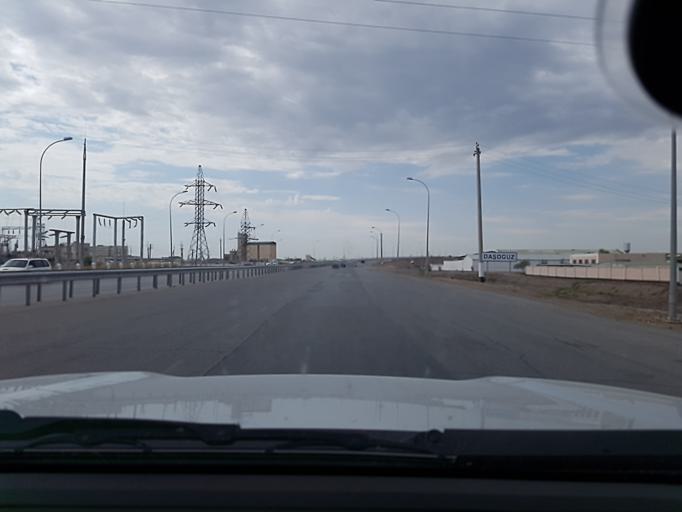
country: TM
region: Dasoguz
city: Dasoguz
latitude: 41.8697
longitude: 59.9501
